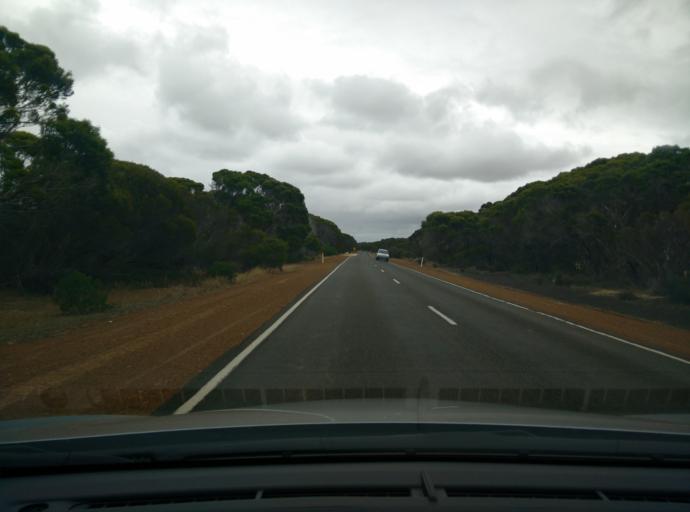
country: AU
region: South Australia
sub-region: Kangaroo Island
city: Kingscote
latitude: -35.7138
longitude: 137.5621
